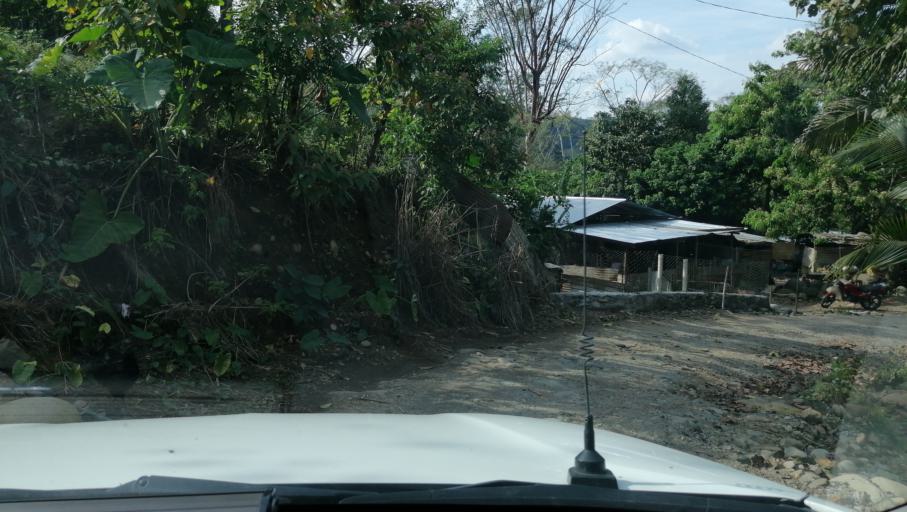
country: MX
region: Chiapas
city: Ostuacan
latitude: 17.4580
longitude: -93.2415
